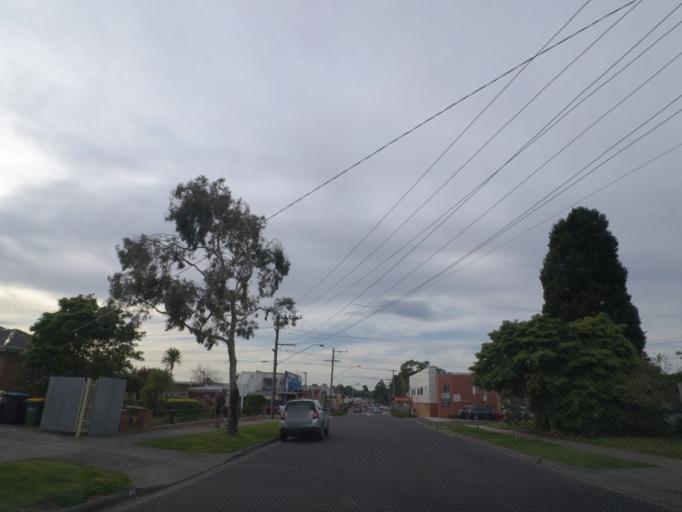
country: AU
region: Victoria
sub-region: Knox
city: Ferntree Gully
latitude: -37.8847
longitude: 145.2759
